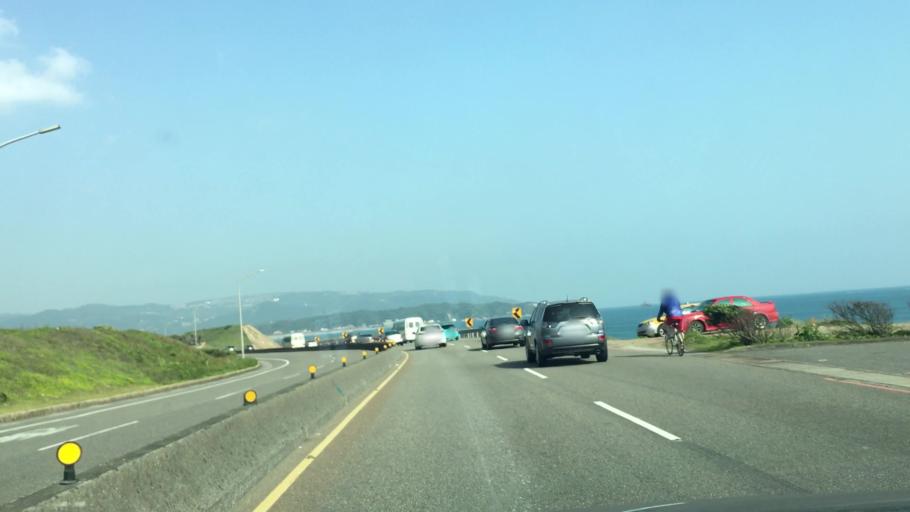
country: TW
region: Taiwan
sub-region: Keelung
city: Keelung
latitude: 25.2018
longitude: 121.6708
